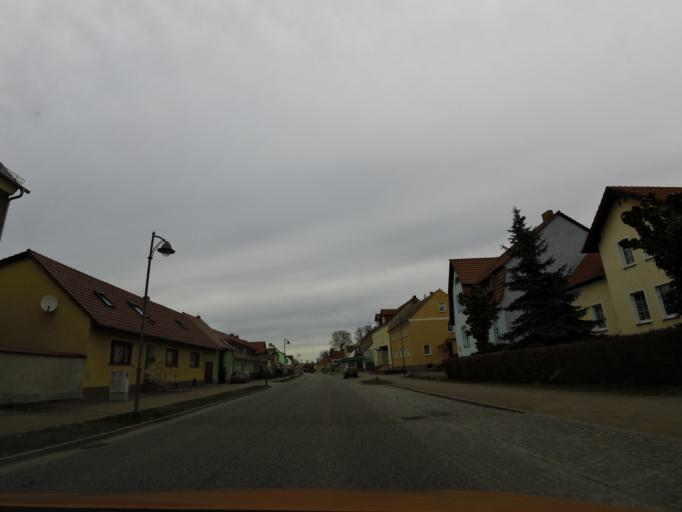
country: DE
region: Brandenburg
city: Bruck
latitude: 52.1923
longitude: 12.7592
